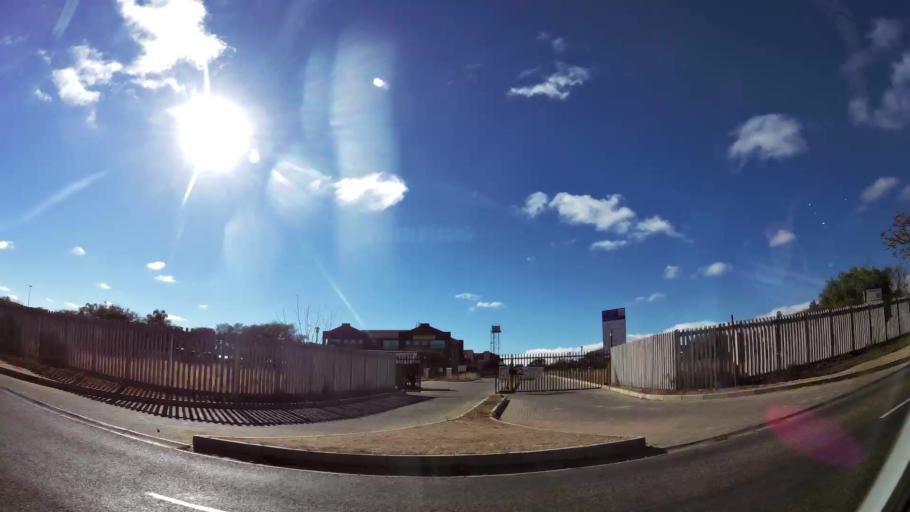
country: ZA
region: Limpopo
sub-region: Capricorn District Municipality
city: Polokwane
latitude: -23.8931
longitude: 29.4562
